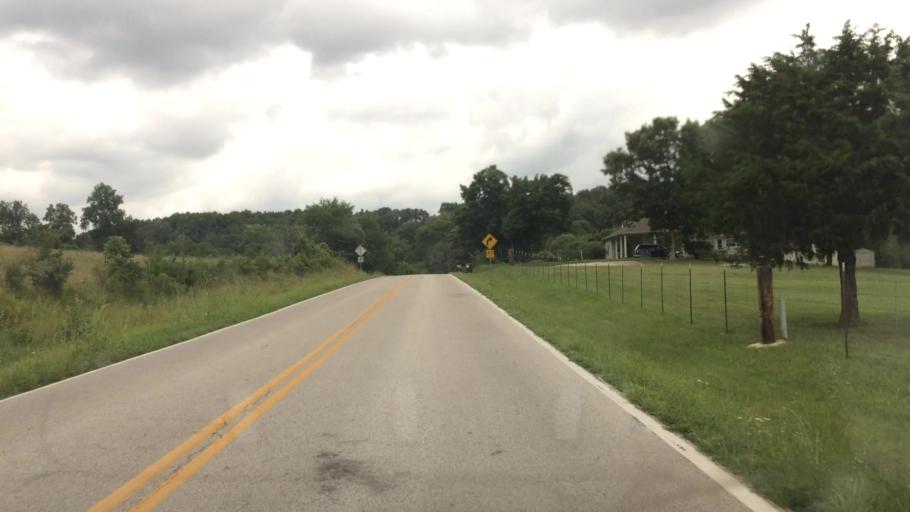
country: US
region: Missouri
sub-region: Greene County
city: Strafford
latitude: 37.2944
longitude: -93.0855
